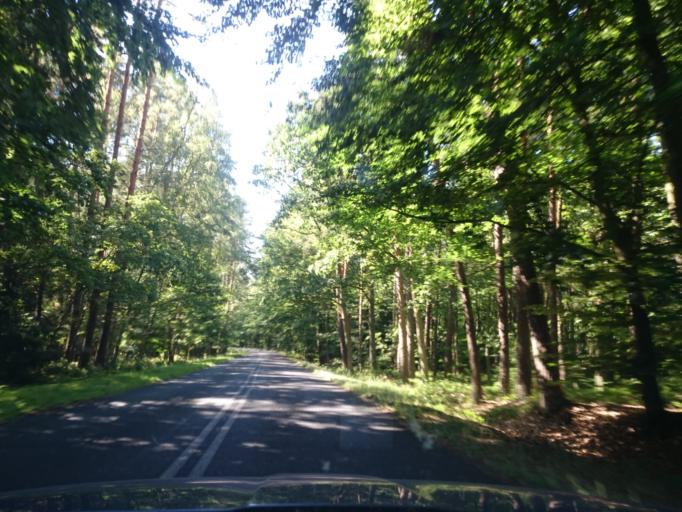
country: PL
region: West Pomeranian Voivodeship
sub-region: Powiat policki
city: Nowe Warpno
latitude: 53.6700
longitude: 14.4166
